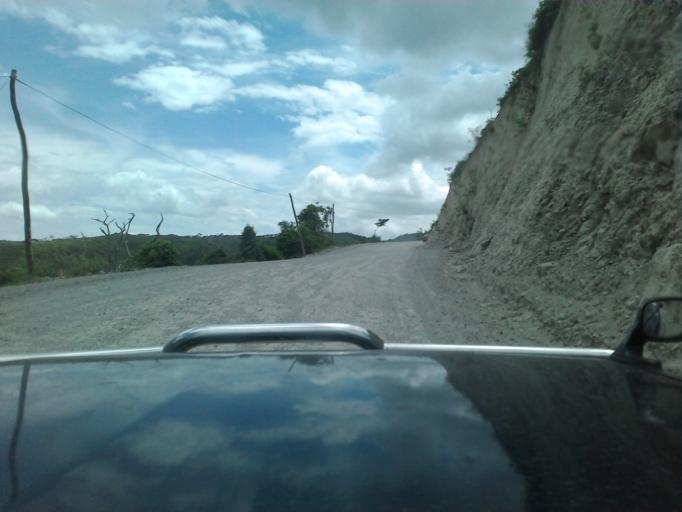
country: CR
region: Guanacaste
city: Juntas
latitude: 10.2586
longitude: -84.8417
